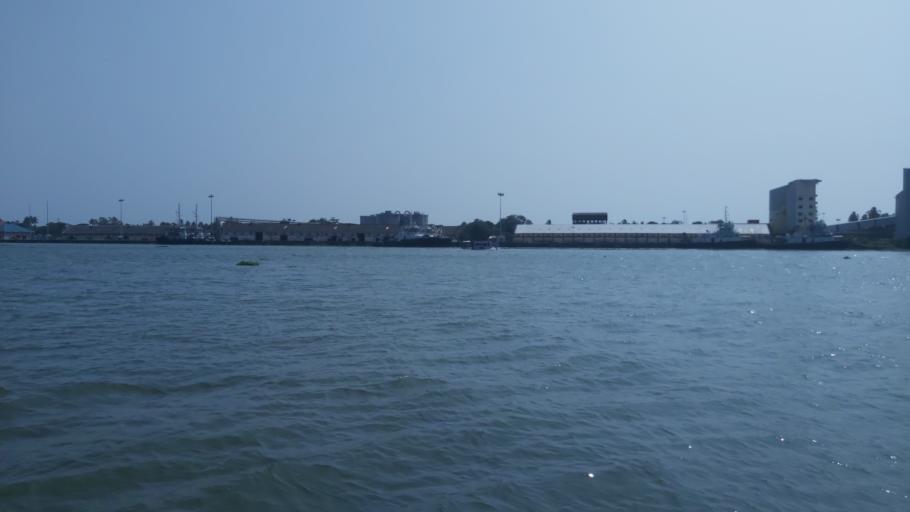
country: IN
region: Kerala
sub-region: Ernakulam
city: Cochin
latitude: 9.9718
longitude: 76.2659
